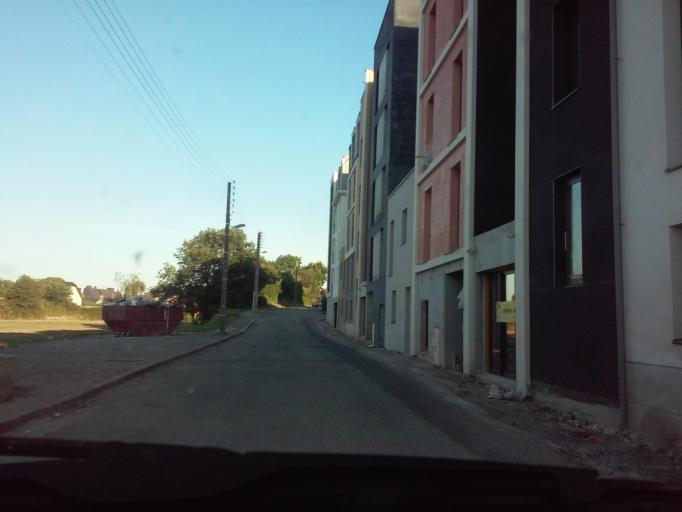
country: FR
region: Brittany
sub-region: Departement d'Ille-et-Vilaine
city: Dinard
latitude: 48.6285
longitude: -2.0641
